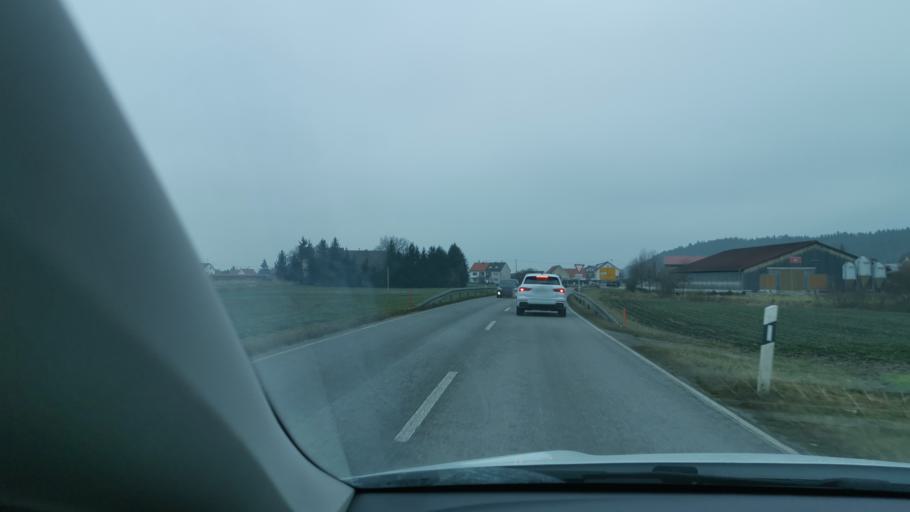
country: DE
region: Bavaria
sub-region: Swabia
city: Todtenweis
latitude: 48.5124
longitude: 10.9174
